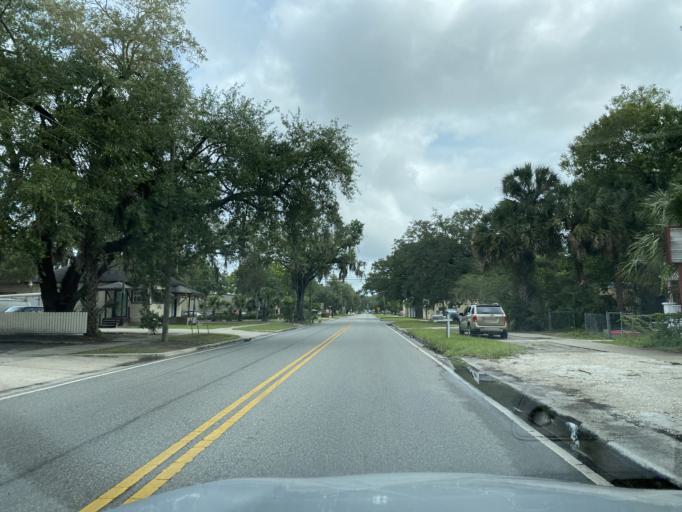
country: US
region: Florida
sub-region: Seminole County
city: Sanford
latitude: 28.8019
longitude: -81.2649
